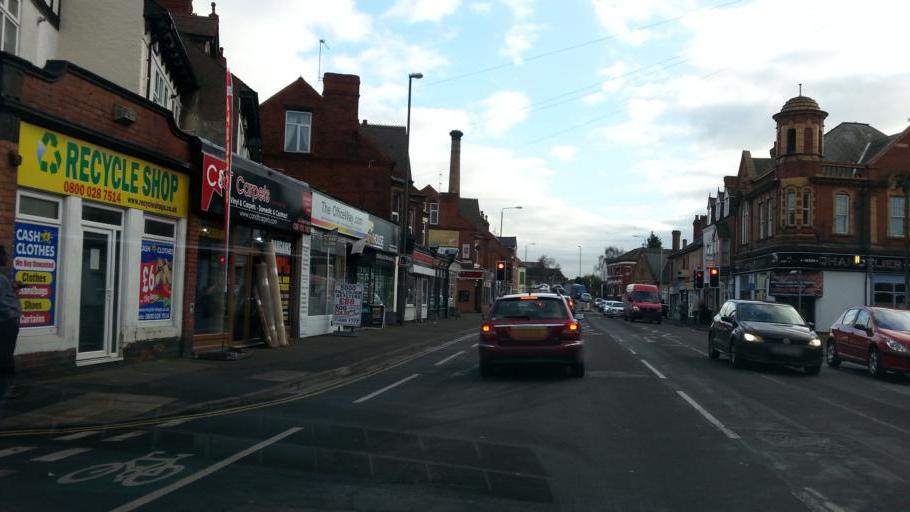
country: GB
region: England
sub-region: Derbyshire
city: Long Eaton
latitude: 52.9008
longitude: -1.2775
